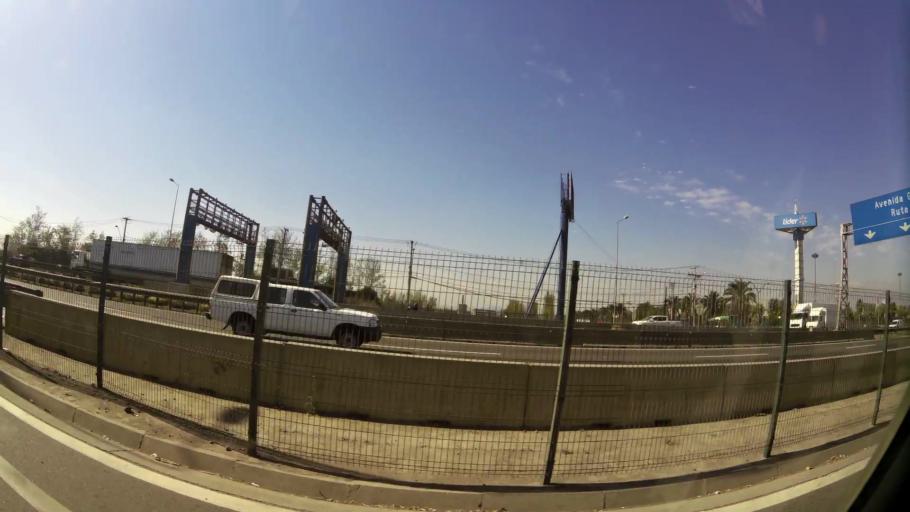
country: CL
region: Santiago Metropolitan
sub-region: Provincia de Santiago
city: Lo Prado
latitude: -33.5170
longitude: -70.7124
